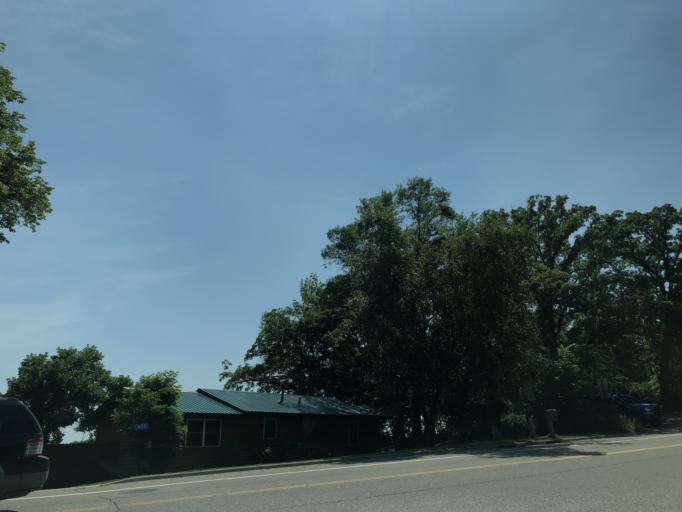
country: US
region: Minnesota
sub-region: Douglas County
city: Alexandria
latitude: 45.9328
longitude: -95.3837
